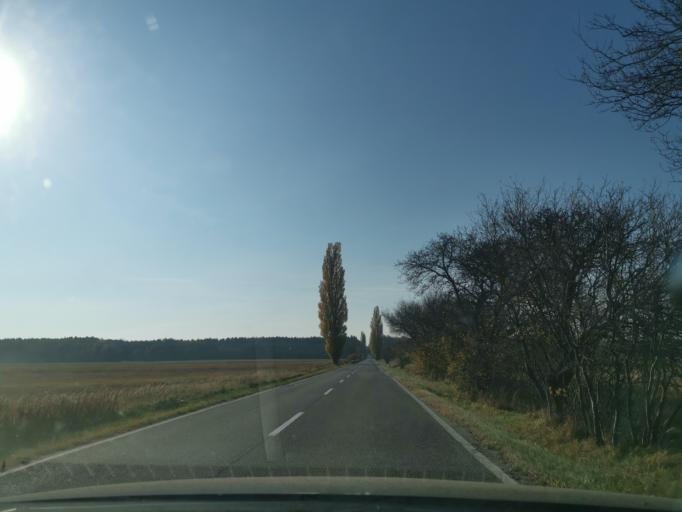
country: SK
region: Trnavsky
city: Gbely
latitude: 48.5676
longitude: 17.1481
